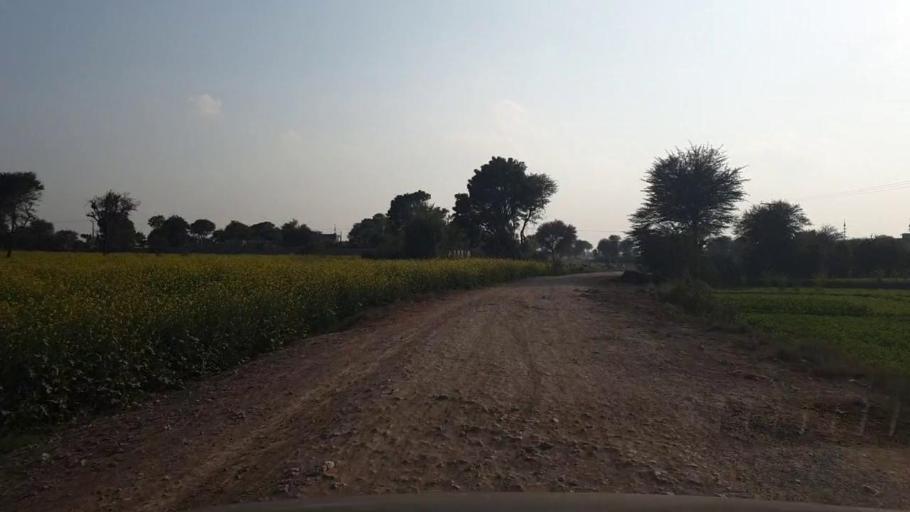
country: PK
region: Sindh
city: Bhit Shah
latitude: 25.7747
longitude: 68.4664
